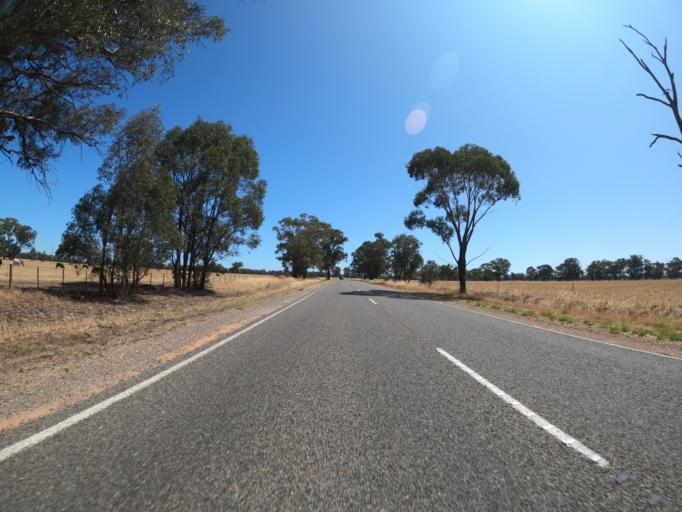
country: AU
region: New South Wales
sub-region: Corowa Shire
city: Corowa
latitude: -36.0750
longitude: 146.3483
